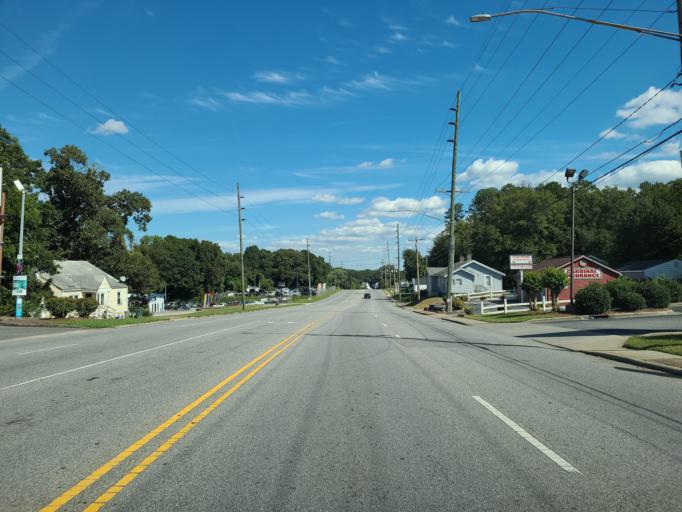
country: US
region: North Carolina
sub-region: Gaston County
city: Gastonia
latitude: 35.2576
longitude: -81.2072
